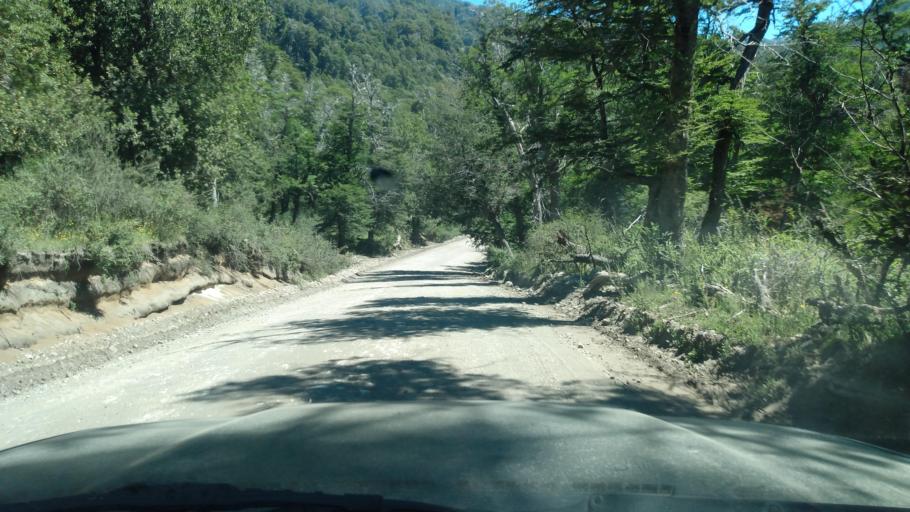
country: AR
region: Neuquen
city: Villa La Angostura
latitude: -40.6223
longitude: -71.5789
